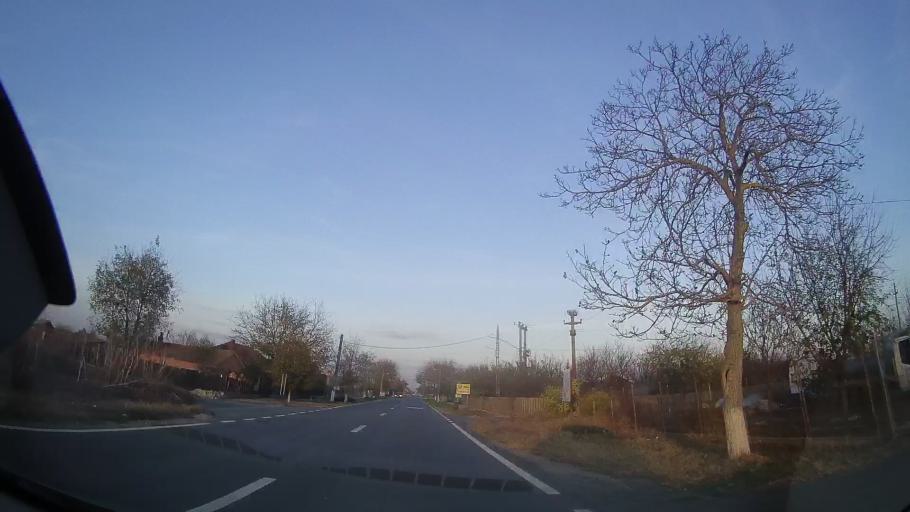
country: RO
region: Constanta
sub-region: Comuna Topraisar
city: Topraisar
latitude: 44.0074
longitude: 28.4434
